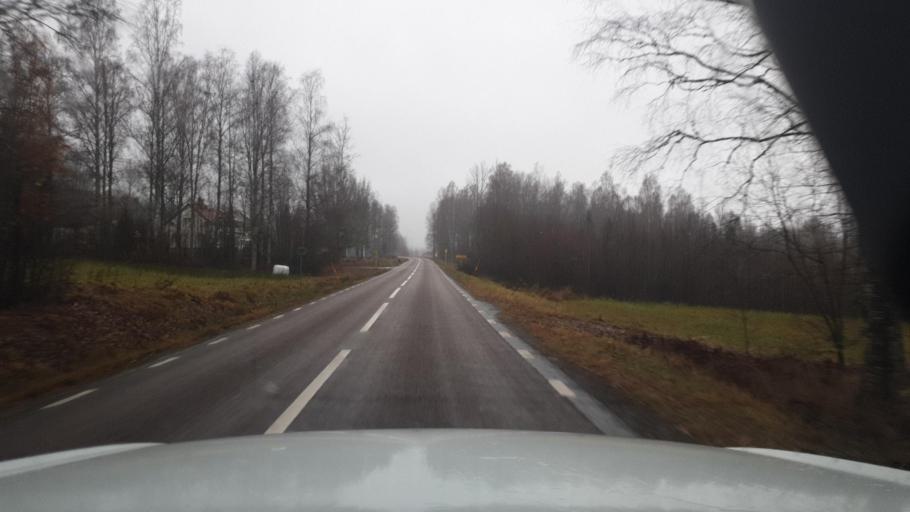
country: SE
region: Vaermland
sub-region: Torsby Kommun
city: Torsby
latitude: 59.9104
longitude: 12.9052
